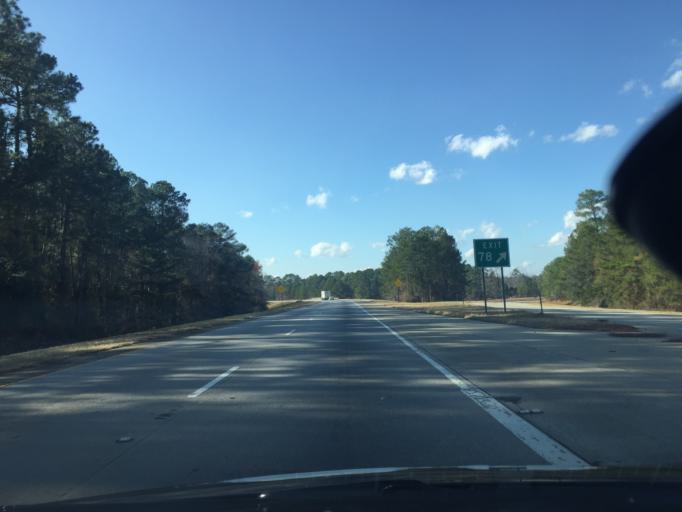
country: US
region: Georgia
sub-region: Treutlen County
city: Soperton
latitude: 32.4345
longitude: -82.4970
